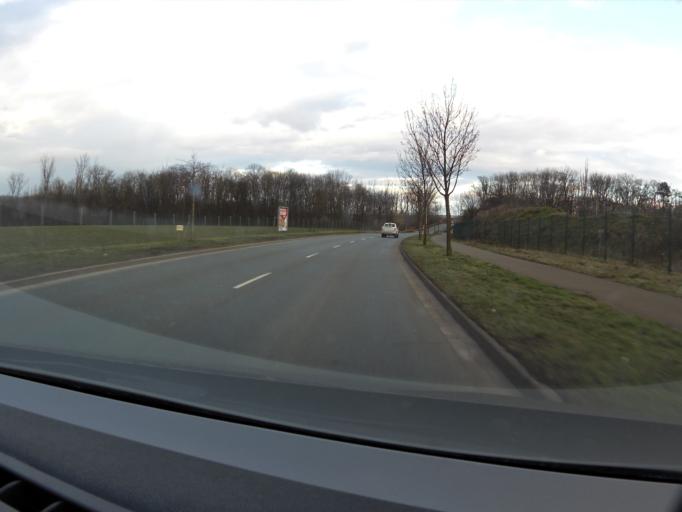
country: DE
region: Thuringia
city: Arnstadt
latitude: 50.8520
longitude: 10.9591
